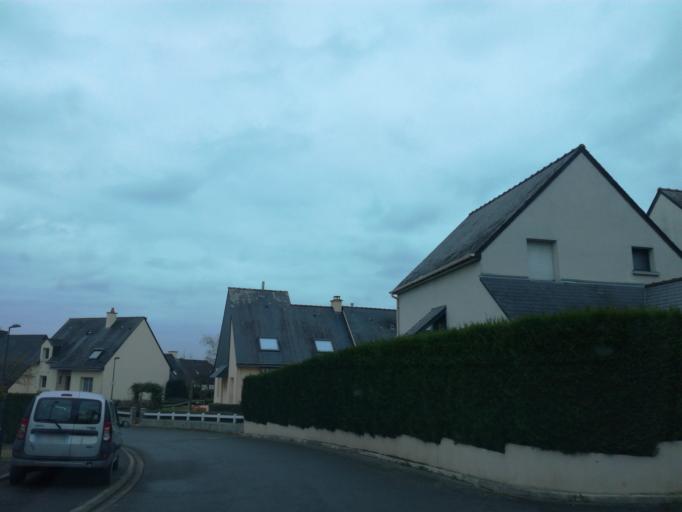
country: FR
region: Brittany
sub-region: Departement d'Ille-et-Vilaine
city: Chantepie
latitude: 48.0838
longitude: -1.6162
